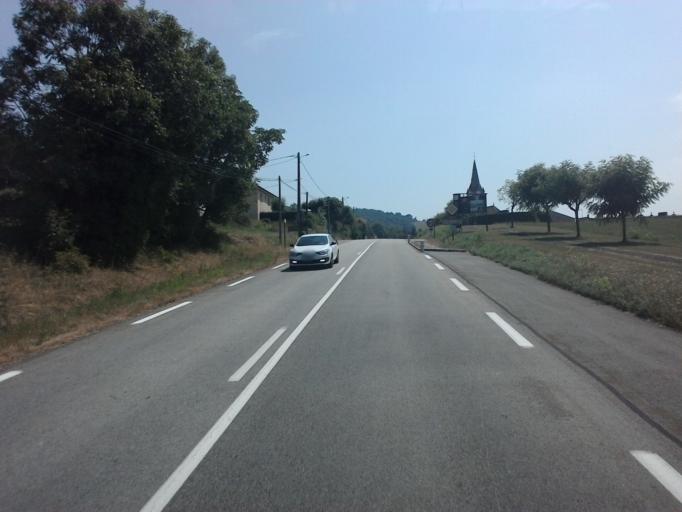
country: FR
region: Rhone-Alpes
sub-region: Departement de l'Isere
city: Montferrat
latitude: 45.4916
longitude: 5.5929
